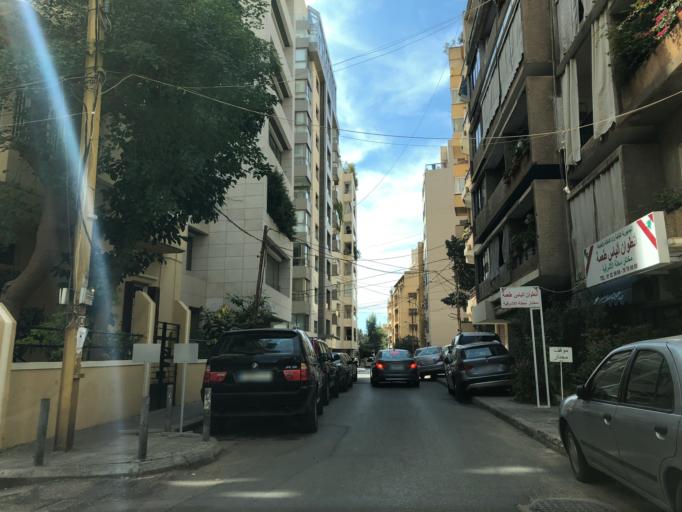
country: LB
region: Beyrouth
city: Beirut
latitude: 33.8858
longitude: 35.5184
